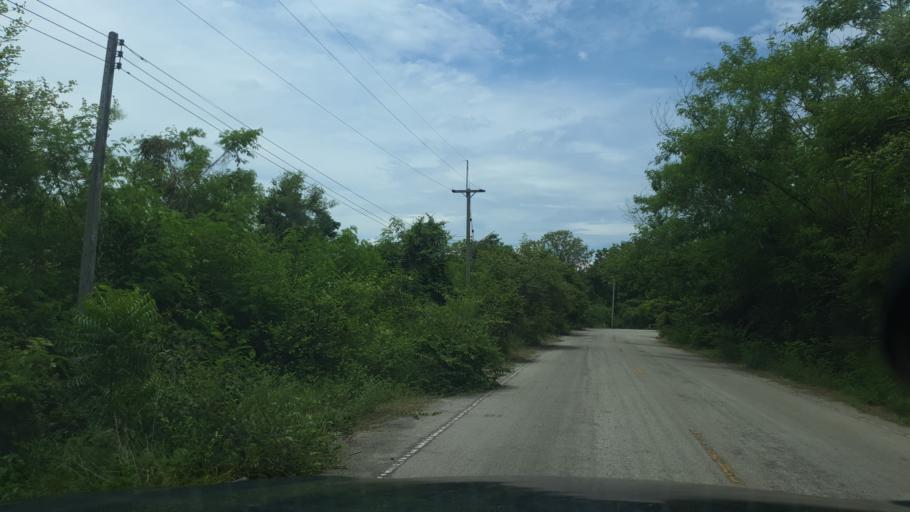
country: TH
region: Lampang
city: Ko Kha
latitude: 18.2534
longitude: 99.3708
